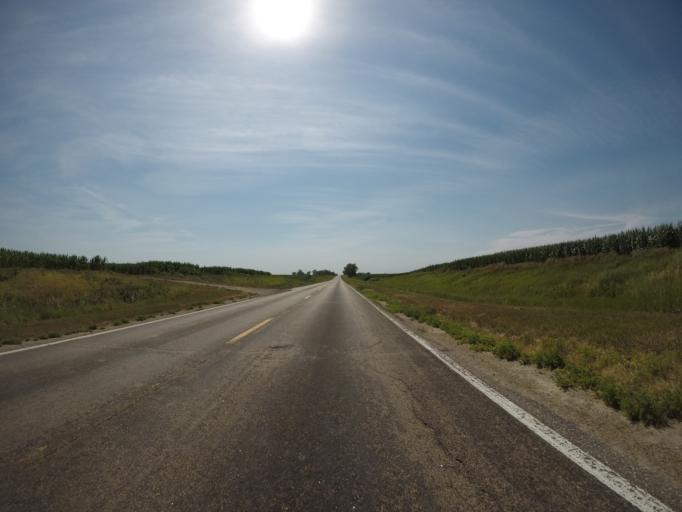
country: US
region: Nebraska
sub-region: Adams County
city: Hastings
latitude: 40.4375
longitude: -98.4711
